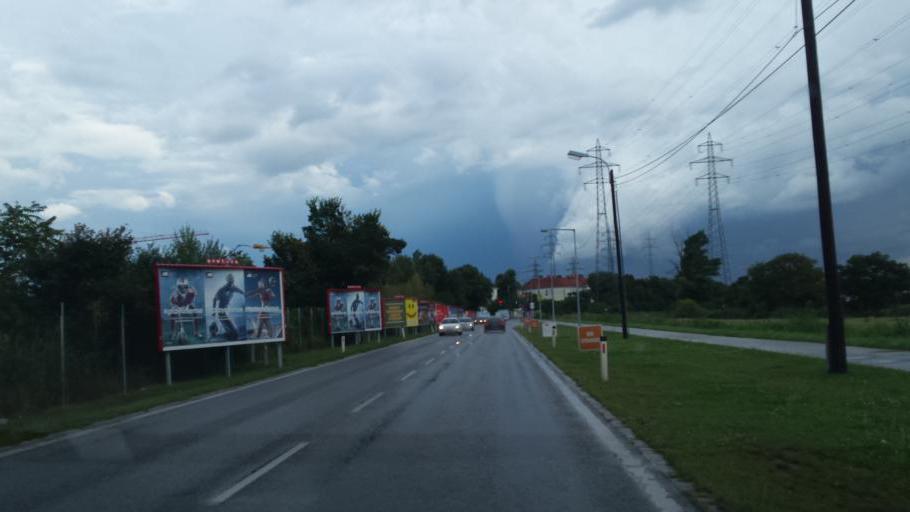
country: AT
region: Lower Austria
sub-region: Politischer Bezirk Wien-Umgebung
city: Schwechat
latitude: 48.1683
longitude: 16.4659
